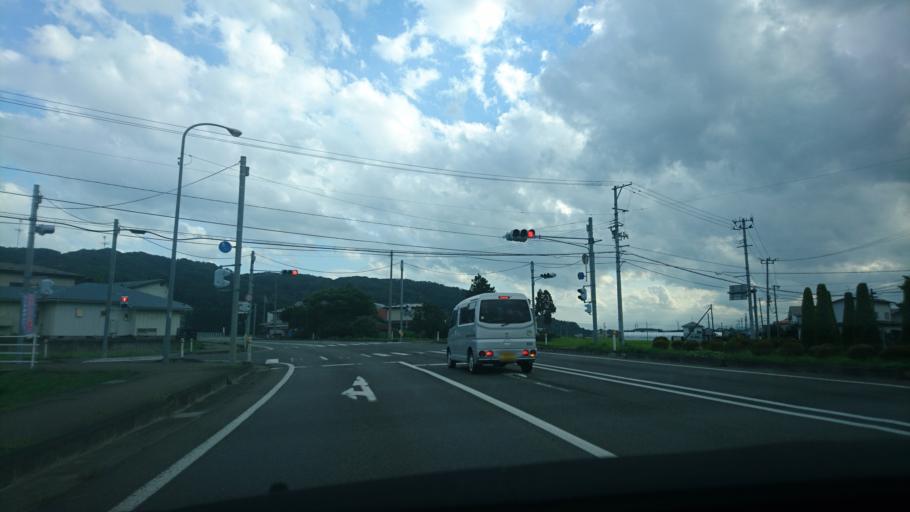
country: JP
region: Iwate
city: Kitakami
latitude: 39.2843
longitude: 141.1370
